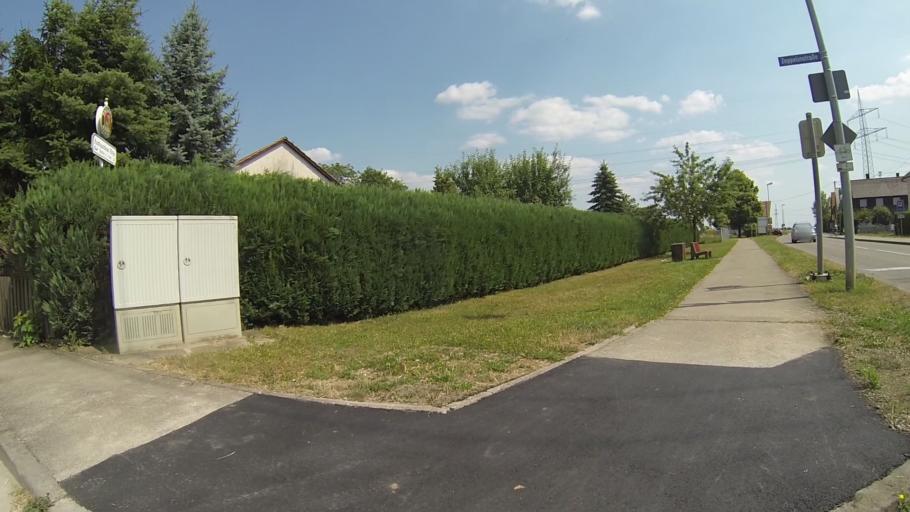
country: DE
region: Baden-Wuerttemberg
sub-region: Regierungsbezirk Stuttgart
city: Niederstotzingen
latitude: 48.5341
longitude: 10.2388
